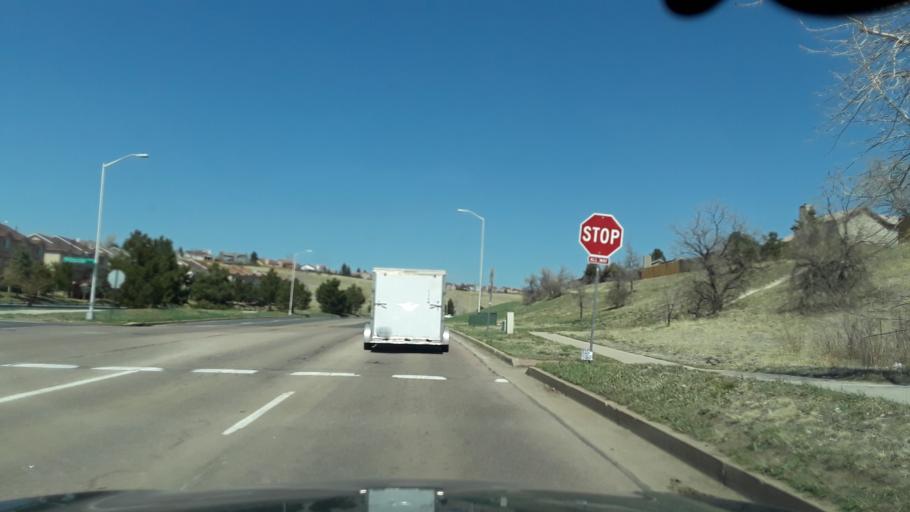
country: US
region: Colorado
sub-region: El Paso County
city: Black Forest
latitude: 38.9454
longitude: -104.7423
